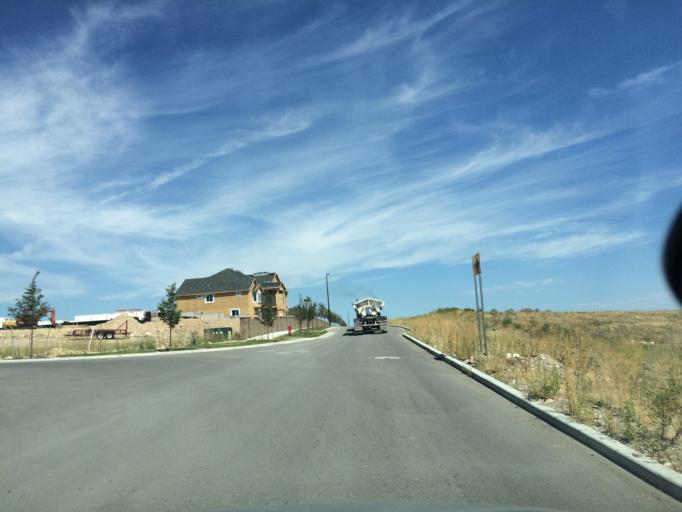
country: US
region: Utah
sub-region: Salt Lake County
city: Oquirrh
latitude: 40.6130
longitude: -112.0436
